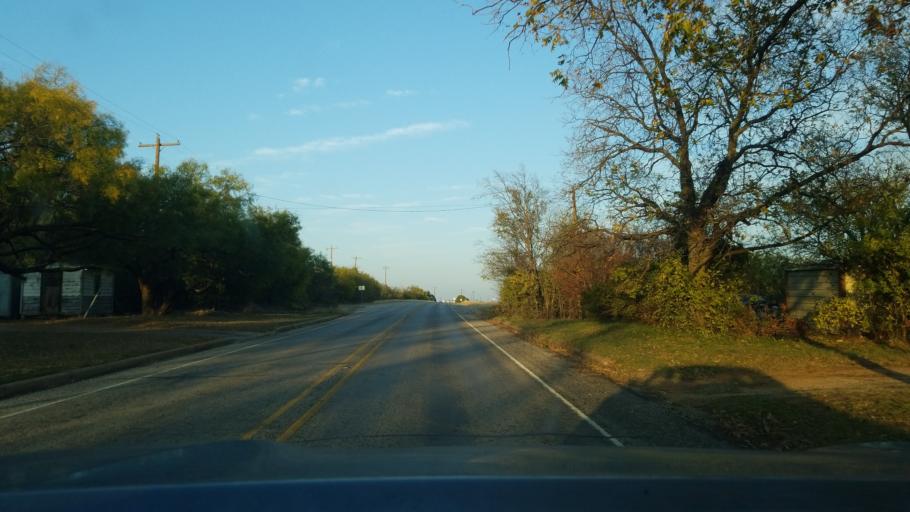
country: US
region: Texas
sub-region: Eastland County
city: Cisco
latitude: 32.3952
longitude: -98.9715
